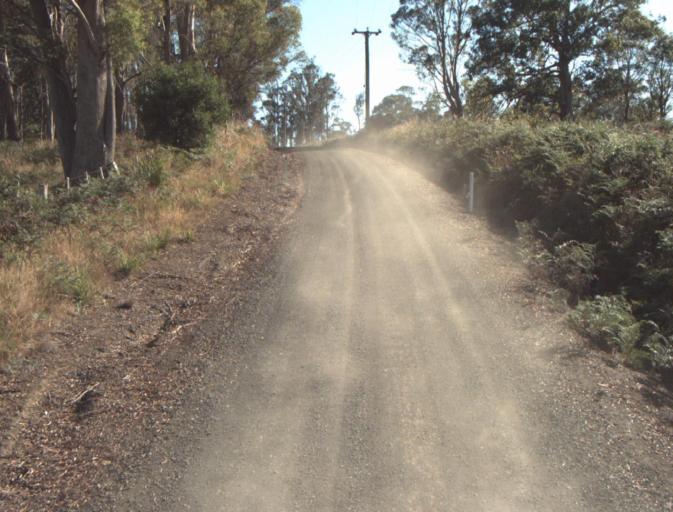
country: AU
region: Tasmania
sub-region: Launceston
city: Newstead
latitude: -41.4150
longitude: 147.2860
